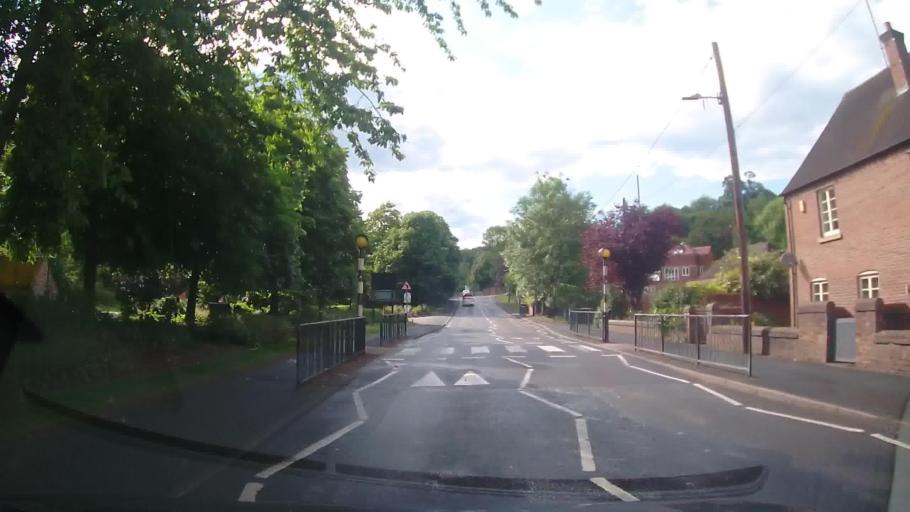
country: GB
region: England
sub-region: Telford and Wrekin
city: Ironbridge
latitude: 52.6304
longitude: -2.4945
